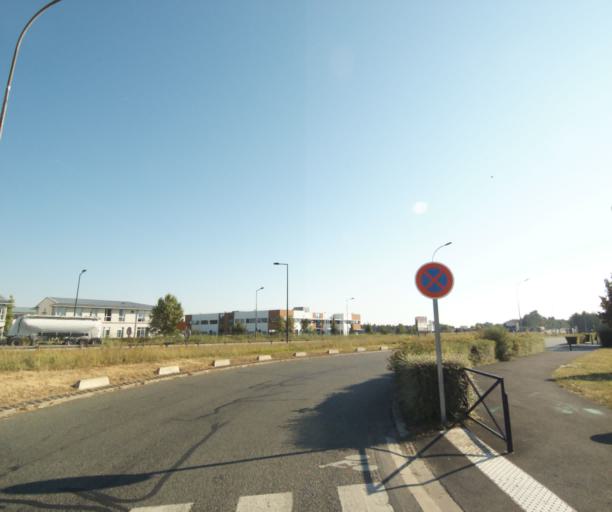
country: FR
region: Ile-de-France
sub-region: Departement de Seine-et-Marne
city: Lieusaint
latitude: 48.6233
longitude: 2.5626
